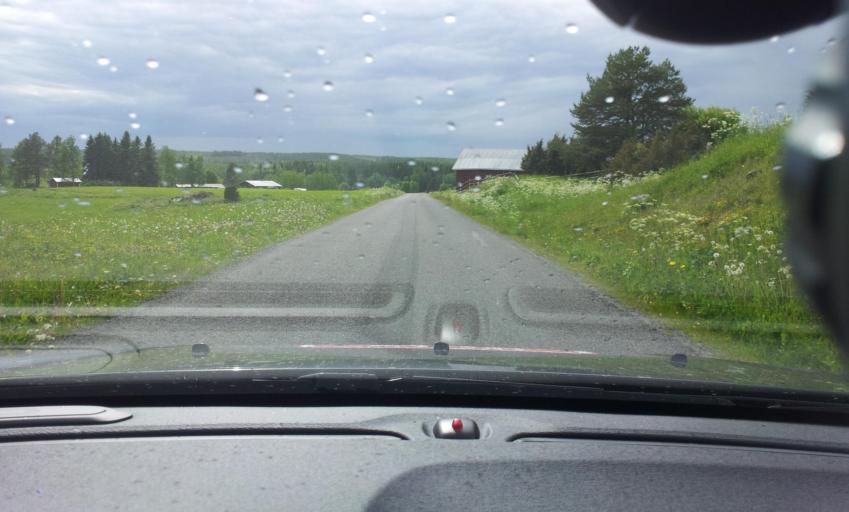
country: SE
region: Jaemtland
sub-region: OEstersunds Kommun
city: Brunflo
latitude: 63.0261
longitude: 14.7894
